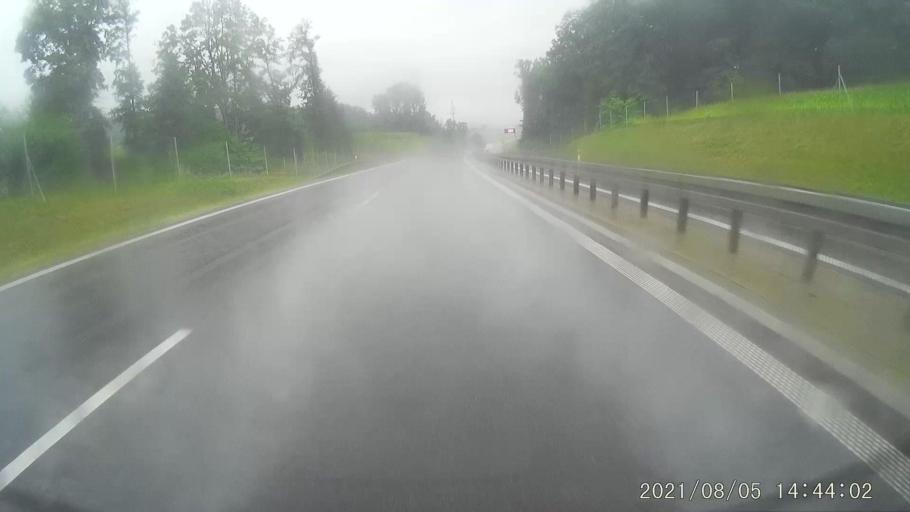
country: PL
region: Opole Voivodeship
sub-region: Powiat nyski
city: Nysa
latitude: 50.4906
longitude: 17.3847
